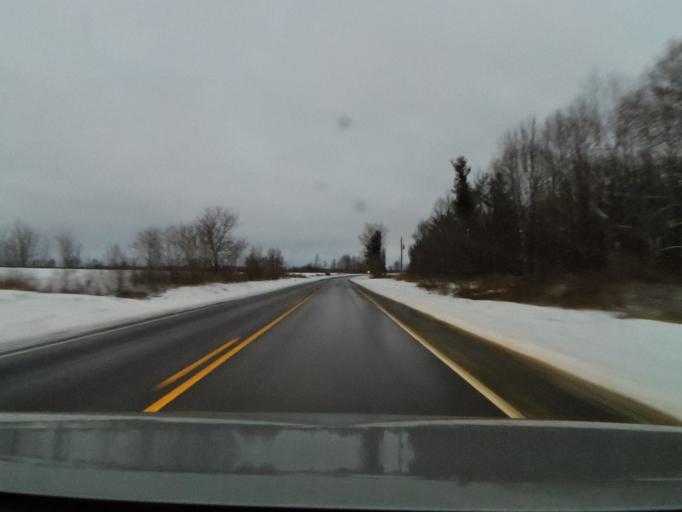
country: US
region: Wisconsin
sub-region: Dunn County
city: Menomonie
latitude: 44.9374
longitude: -92.0105
